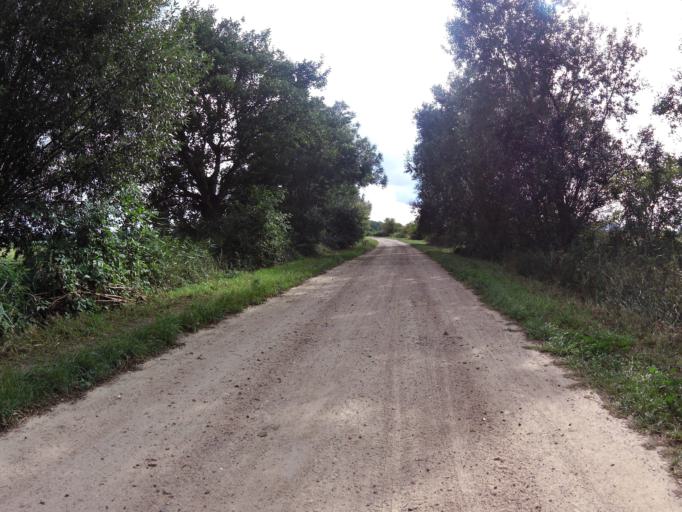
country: DE
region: Mecklenburg-Vorpommern
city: Loddin
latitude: 53.9911
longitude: 14.0579
